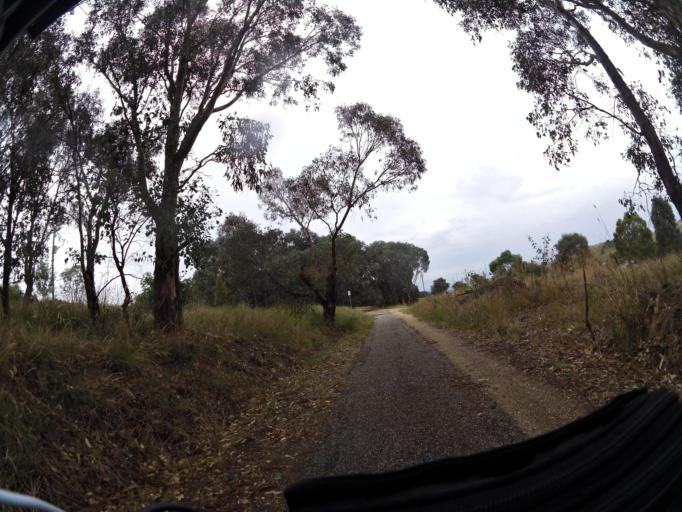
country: AU
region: New South Wales
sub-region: Albury Municipality
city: East Albury
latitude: -36.2245
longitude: 147.1198
